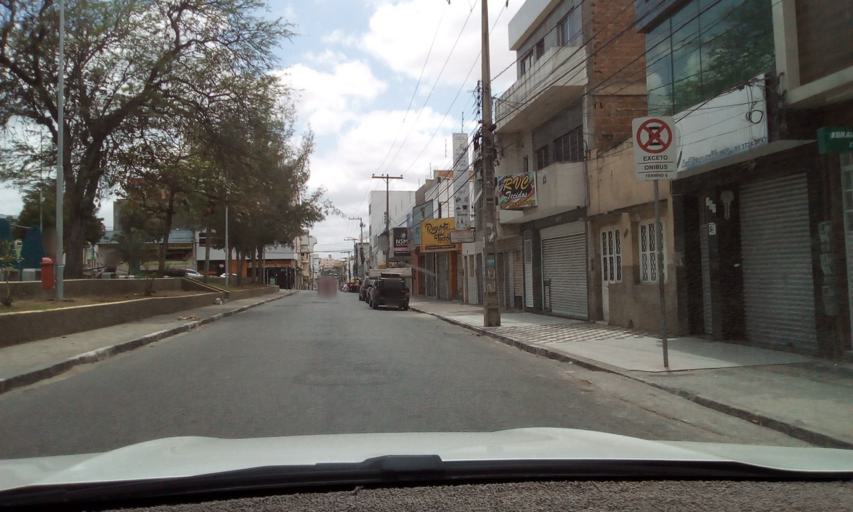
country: BR
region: Pernambuco
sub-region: Caruaru
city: Caruaru
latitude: -8.2882
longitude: -35.9760
